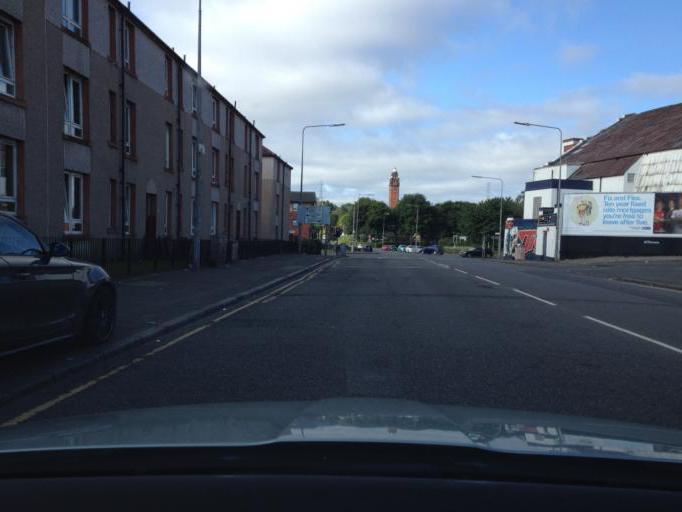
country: GB
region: Scotland
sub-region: Glasgow City
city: Glasgow
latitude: 55.8865
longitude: -4.2556
